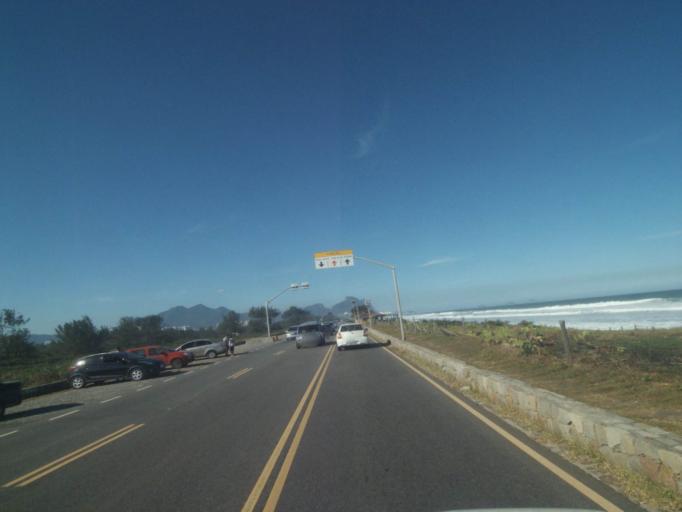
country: BR
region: Rio de Janeiro
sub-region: Nilopolis
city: Nilopolis
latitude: -23.0157
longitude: -43.4126
